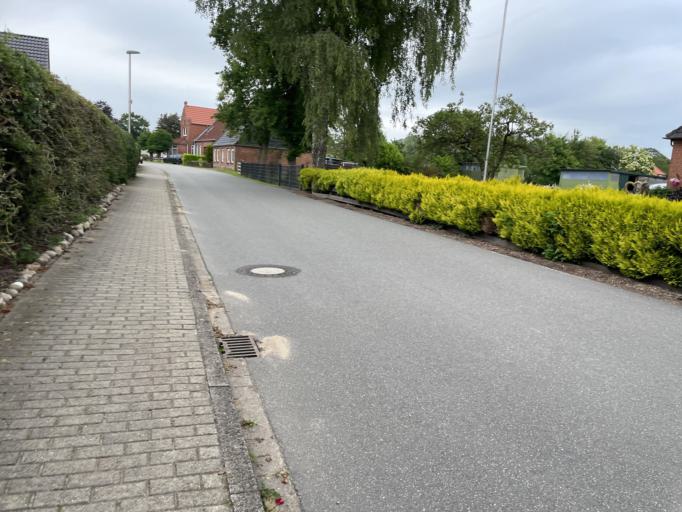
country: DE
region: Schleswig-Holstein
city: Mildstedt
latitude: 54.4602
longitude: 9.0929
